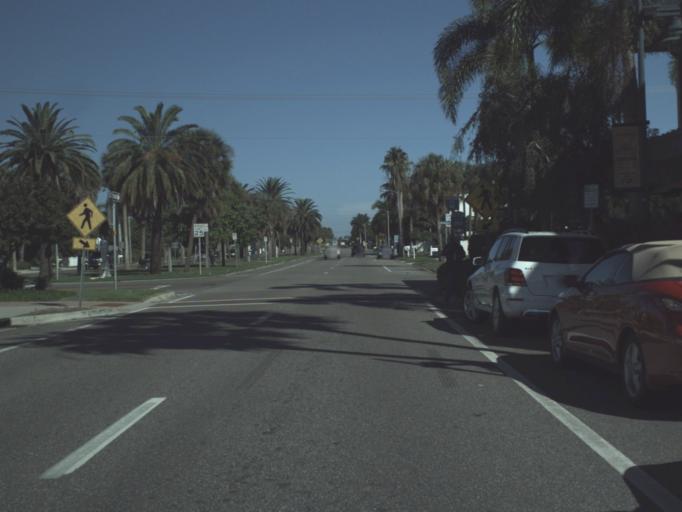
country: US
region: Florida
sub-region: Sarasota County
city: Siesta Key
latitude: 27.3195
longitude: -82.5778
